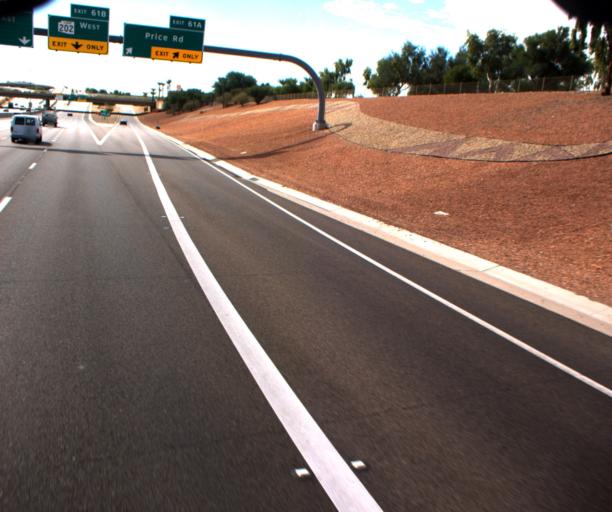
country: US
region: Arizona
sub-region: Maricopa County
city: Chandler
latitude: 33.3019
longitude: -111.8944
